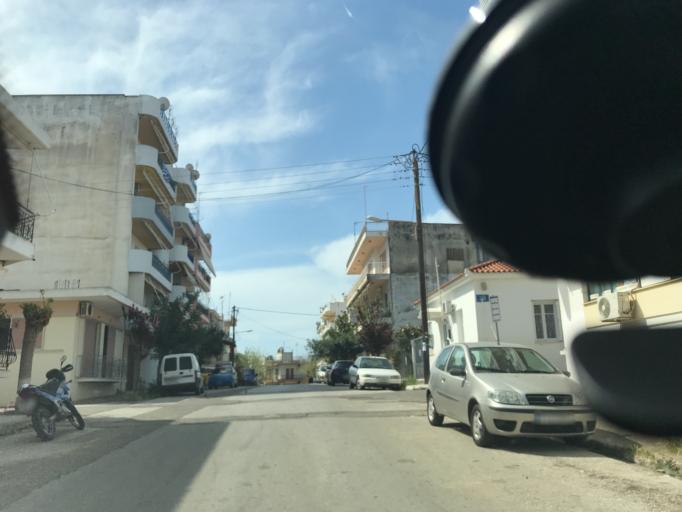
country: GR
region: West Greece
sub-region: Nomos Ileias
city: Pyrgos
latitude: 37.6734
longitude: 21.4466
